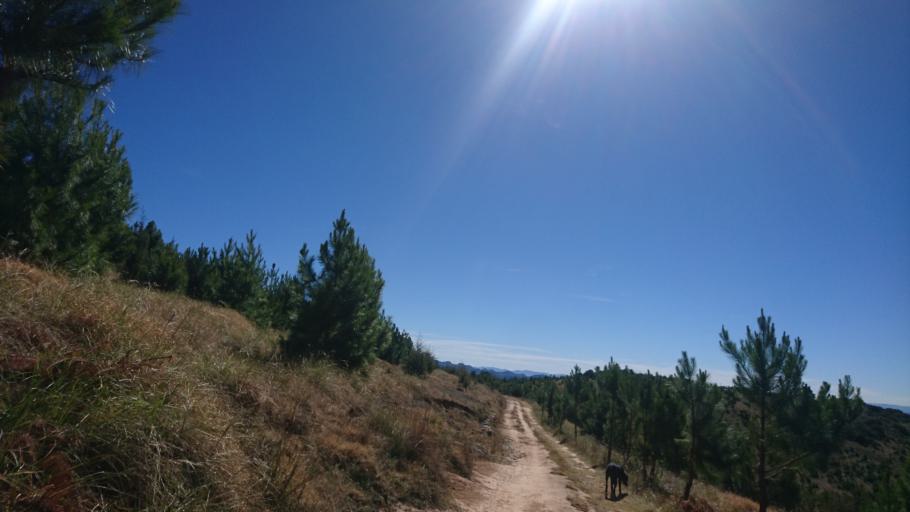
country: MX
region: San Luis Potosi
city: Zaragoza
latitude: 22.0176
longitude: -100.6214
